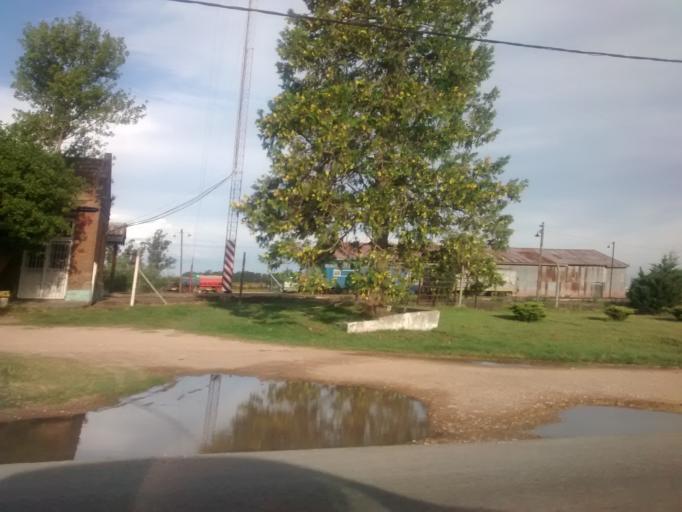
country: AR
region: Buenos Aires
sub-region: Partido de Loberia
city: Loberia
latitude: -38.2025
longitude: -58.7363
